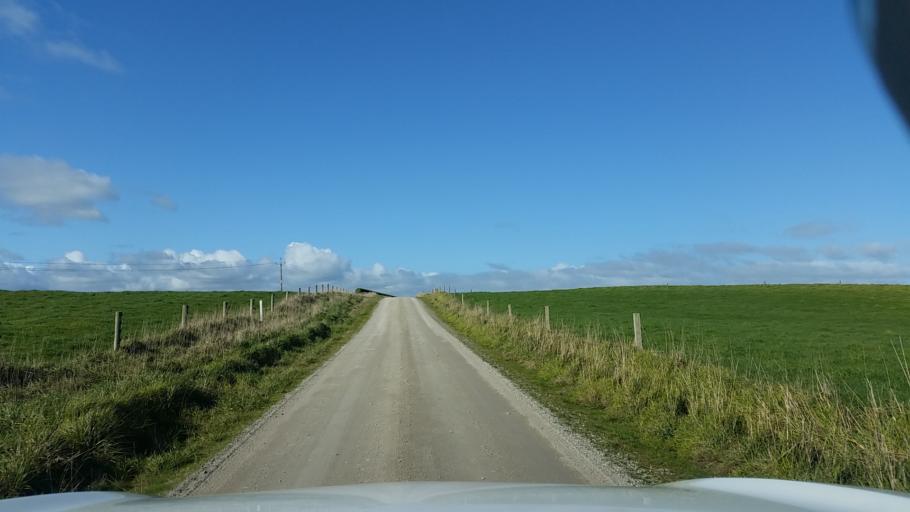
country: NZ
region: Taranaki
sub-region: South Taranaki District
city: Patea
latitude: -39.6849
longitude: 174.3928
